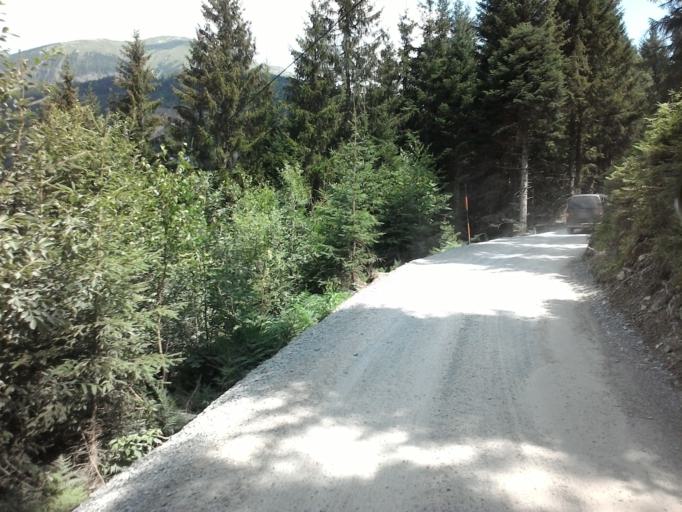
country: AT
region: Tyrol
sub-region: Politischer Bezirk Lienz
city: Untertilliach
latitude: 46.6987
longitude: 12.7710
